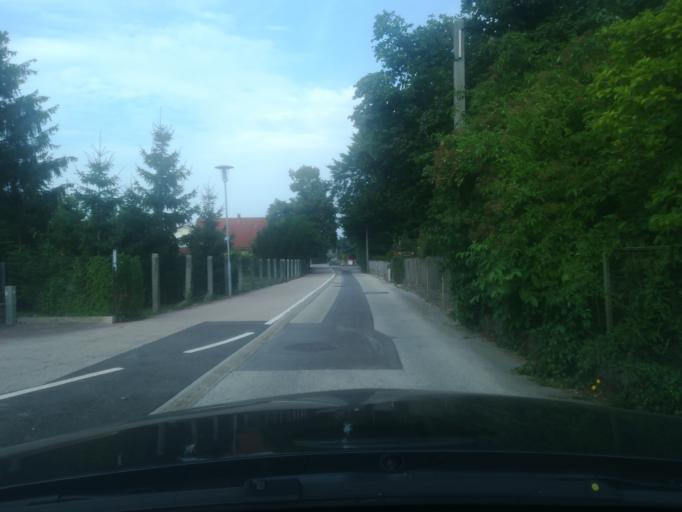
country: AT
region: Upper Austria
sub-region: Wels-Land
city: Marchtrenk
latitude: 48.1961
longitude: 14.1179
